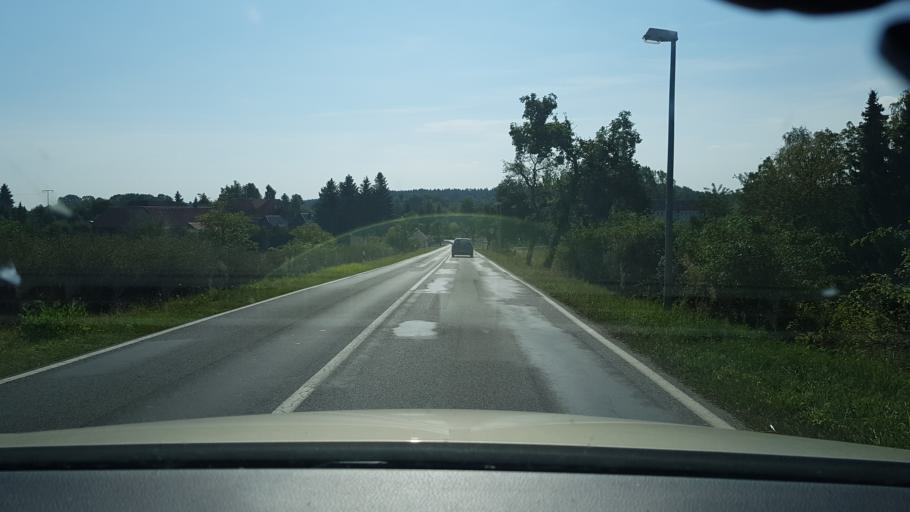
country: DE
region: Brandenburg
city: Lawitz
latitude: 52.1075
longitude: 14.5883
